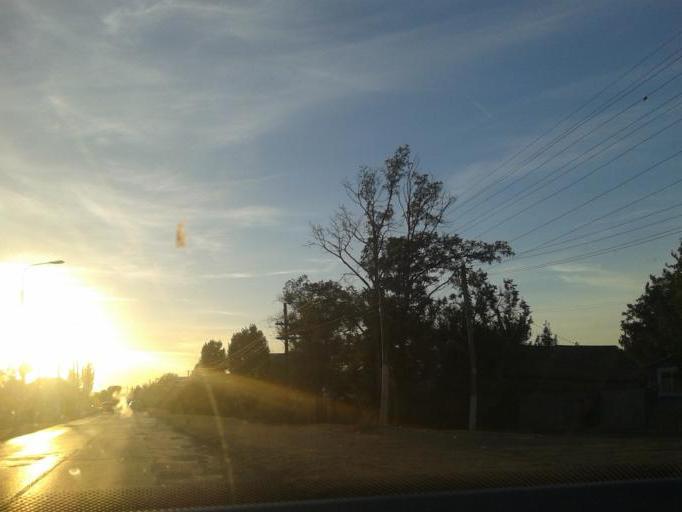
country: RU
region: Volgograd
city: Krasnoslobodsk
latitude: 48.7091
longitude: 44.5766
